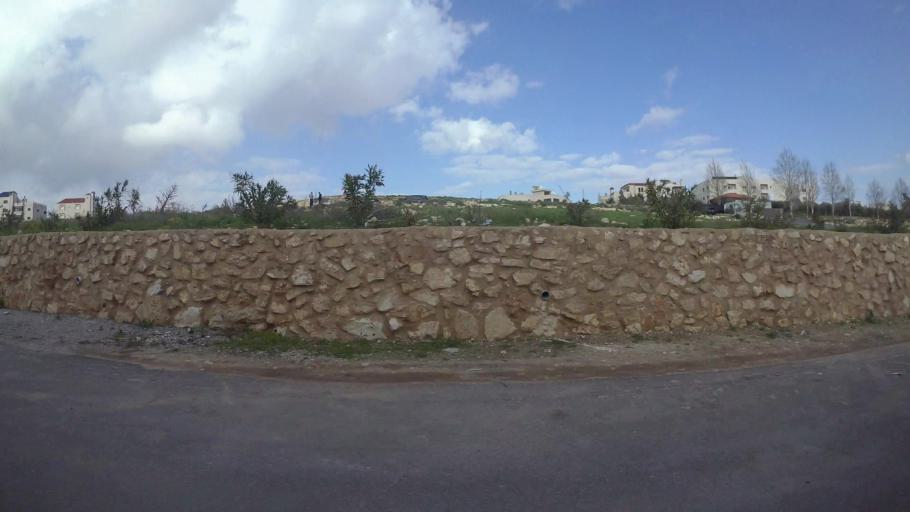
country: JO
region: Amman
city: Al Jubayhah
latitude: 31.9832
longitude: 35.8514
